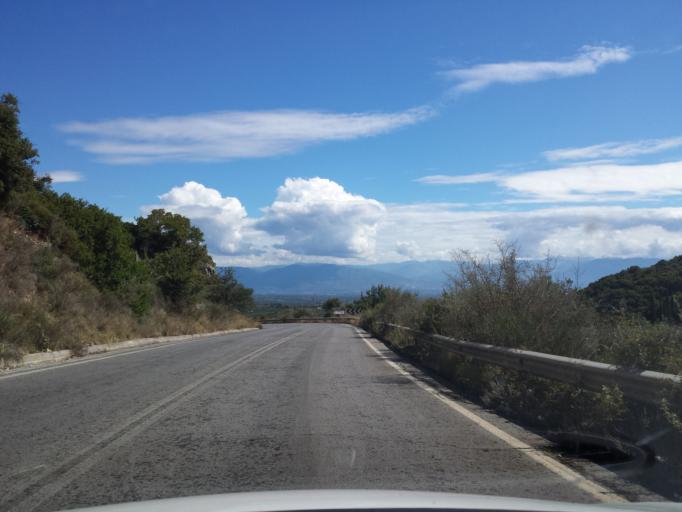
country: GR
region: Peloponnese
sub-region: Nomos Messinias
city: Vlakhopoulon
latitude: 36.9981
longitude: 21.8571
